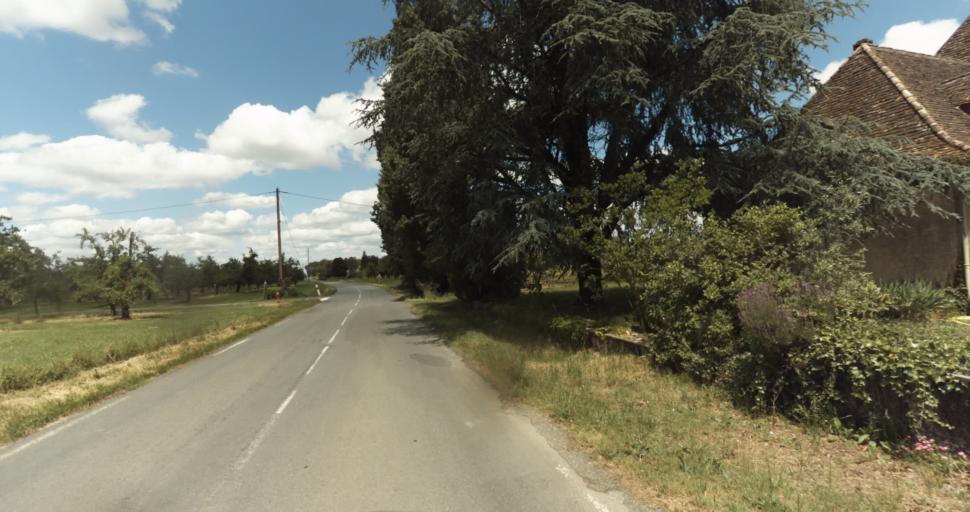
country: FR
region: Aquitaine
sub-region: Departement de la Dordogne
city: Beaumont-du-Perigord
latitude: 44.7389
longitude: 0.7824
